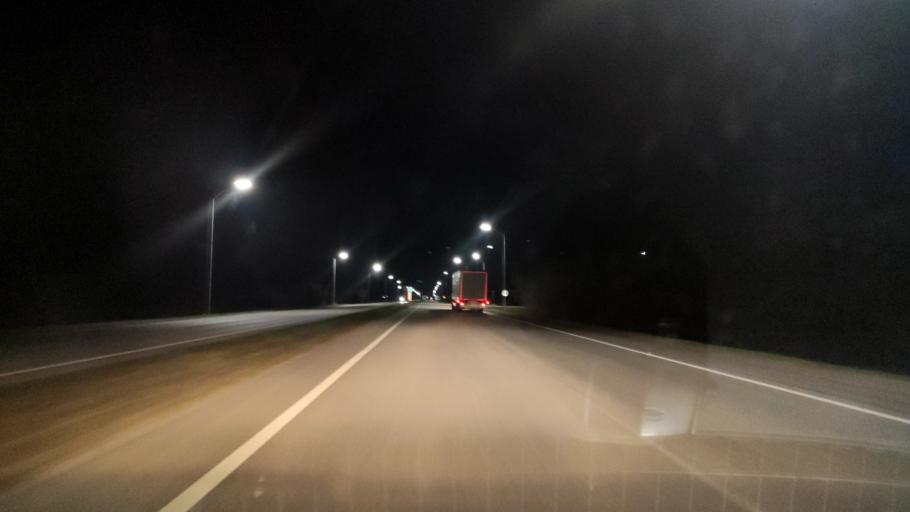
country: RU
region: Belgorod
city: Staryy Oskol
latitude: 51.3708
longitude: 37.8457
